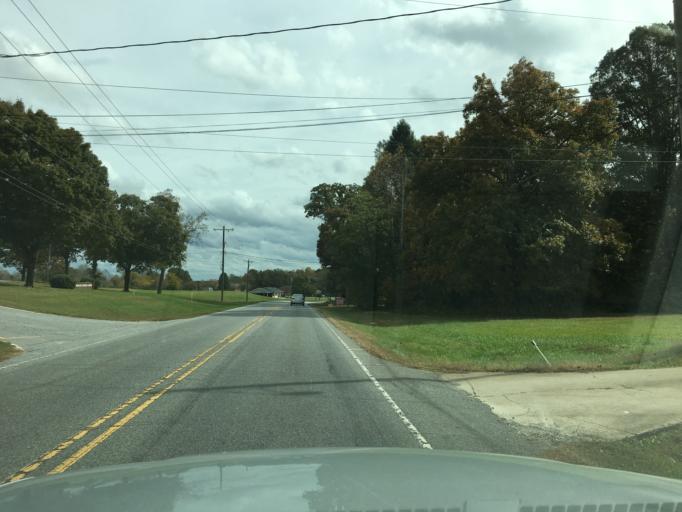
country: US
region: North Carolina
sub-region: Catawba County
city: Newton
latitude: 35.6927
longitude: -81.2852
